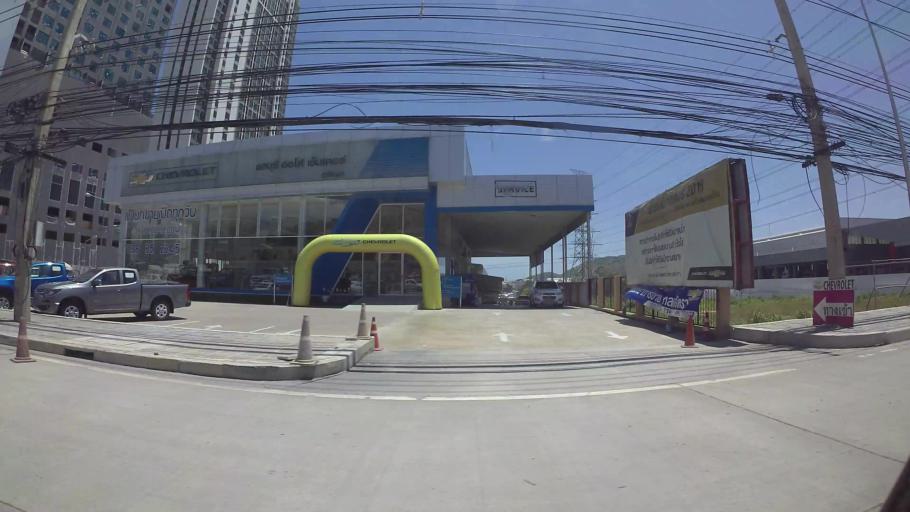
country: TH
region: Chon Buri
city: Si Racha
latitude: 13.1247
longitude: 100.9173
